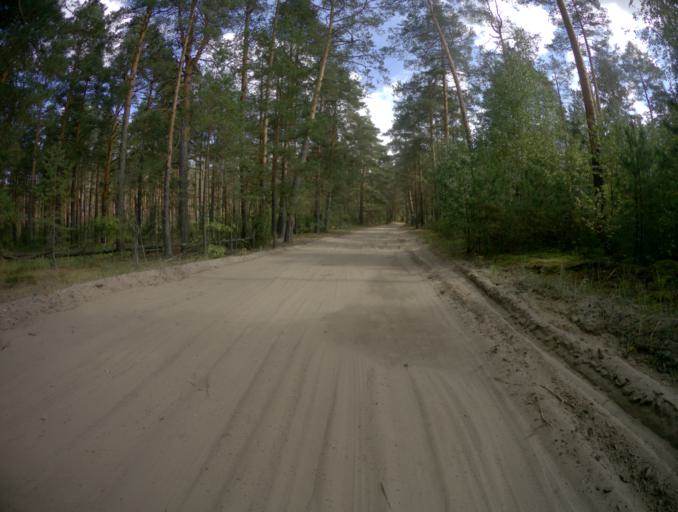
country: RU
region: Vladimir
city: Petushki
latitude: 55.8670
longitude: 39.3265
